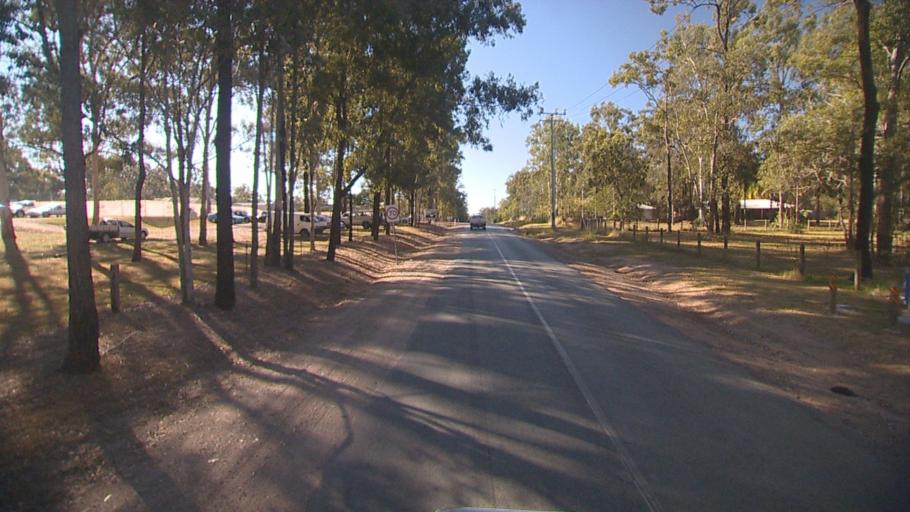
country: AU
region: Queensland
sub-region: Logan
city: North Maclean
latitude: -27.7560
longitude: 153.0132
